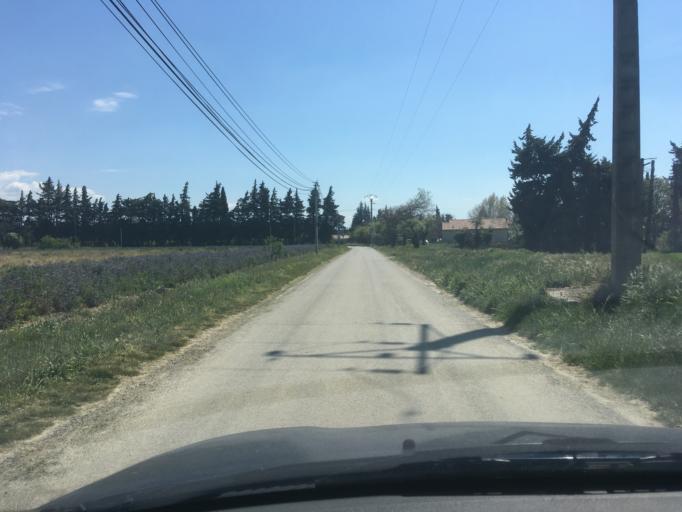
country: FR
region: Provence-Alpes-Cote d'Azur
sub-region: Departement du Vaucluse
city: Jonquieres
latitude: 44.1069
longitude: 4.9369
